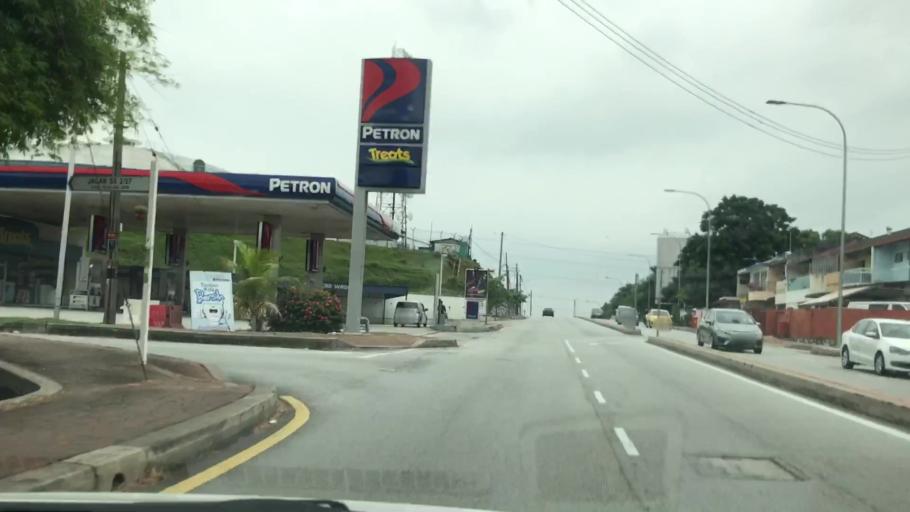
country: MY
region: Selangor
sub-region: Petaling
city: Petaling Jaya
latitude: 3.1121
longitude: 101.6193
